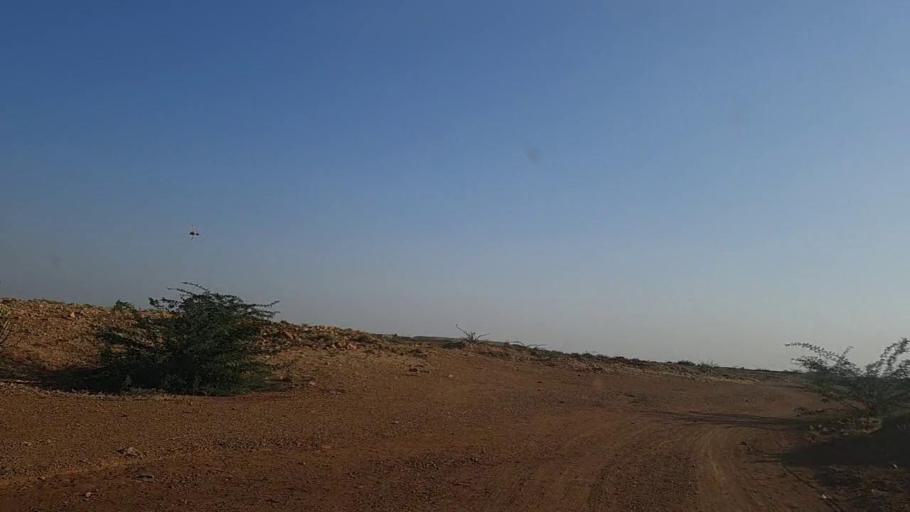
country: PK
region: Sindh
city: Daro Mehar
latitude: 24.9995
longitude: 68.1323
